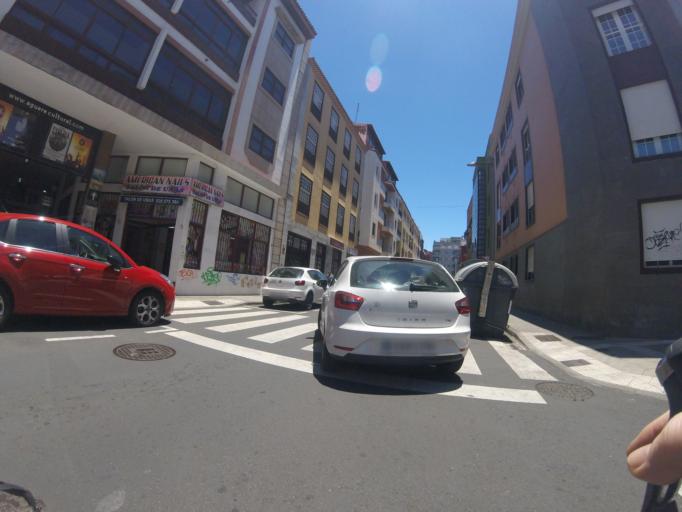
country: ES
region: Canary Islands
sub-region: Provincia de Santa Cruz de Tenerife
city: La Laguna
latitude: 28.4870
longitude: -16.3174
